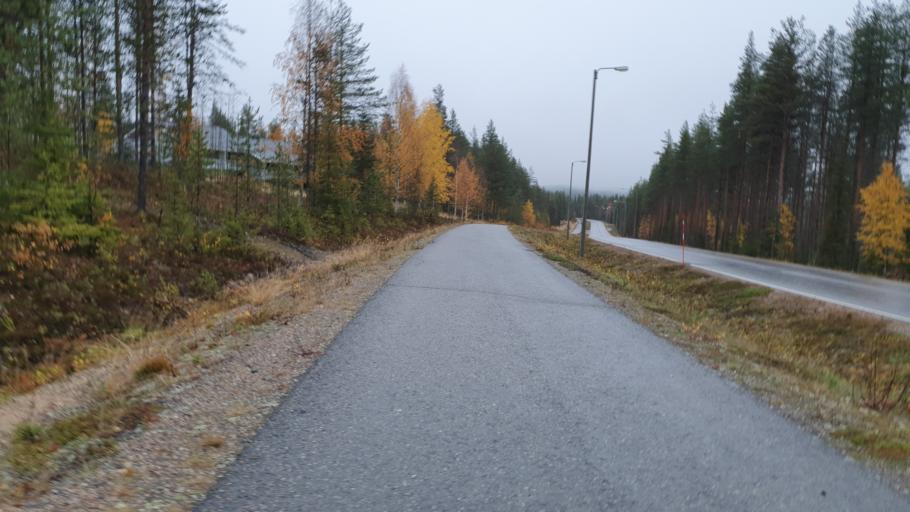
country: FI
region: Lapland
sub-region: Tunturi-Lappi
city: Kolari
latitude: 67.6010
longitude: 24.1263
